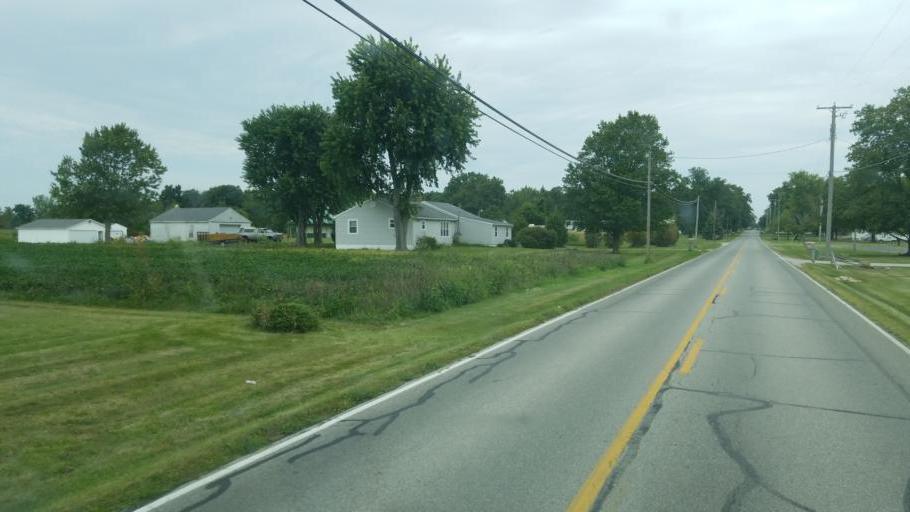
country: US
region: Ohio
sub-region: Marion County
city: Marion
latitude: 40.5401
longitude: -83.1368
